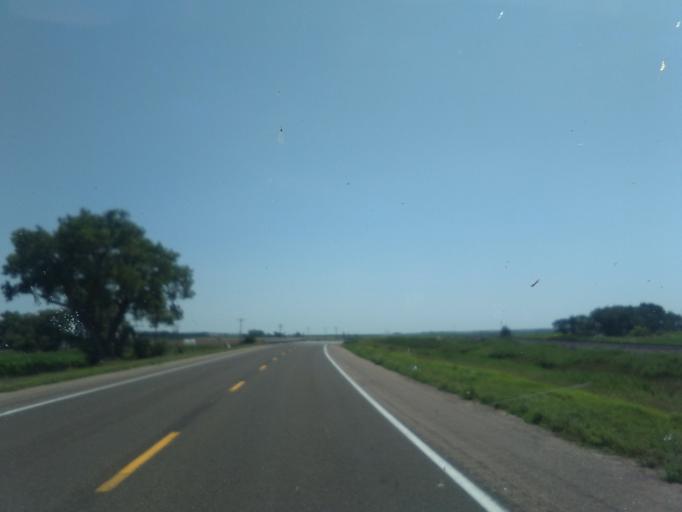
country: US
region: Nebraska
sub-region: Dundy County
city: Benkelman
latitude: 40.1253
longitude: -101.3608
